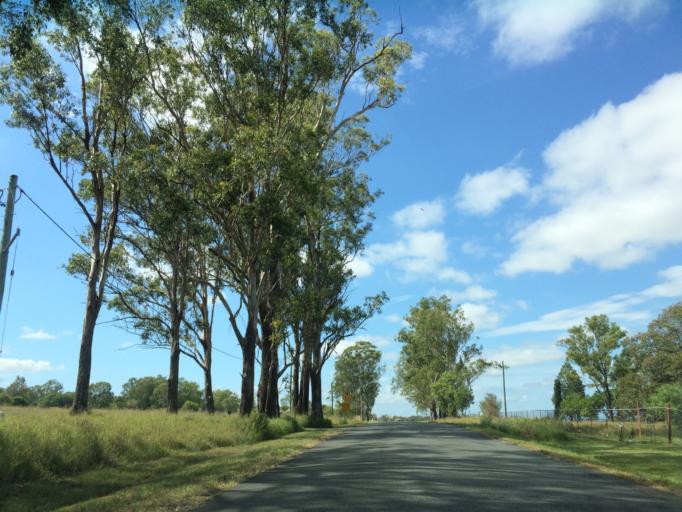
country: AU
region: Queensland
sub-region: Logan
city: Cedar Vale
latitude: -27.8857
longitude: 152.9724
